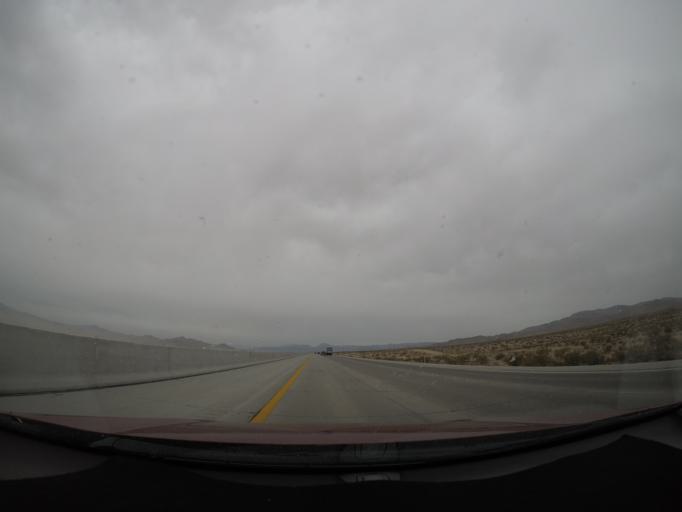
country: US
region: Nevada
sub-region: Clark County
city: Enterprise
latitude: 35.8605
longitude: -115.2551
